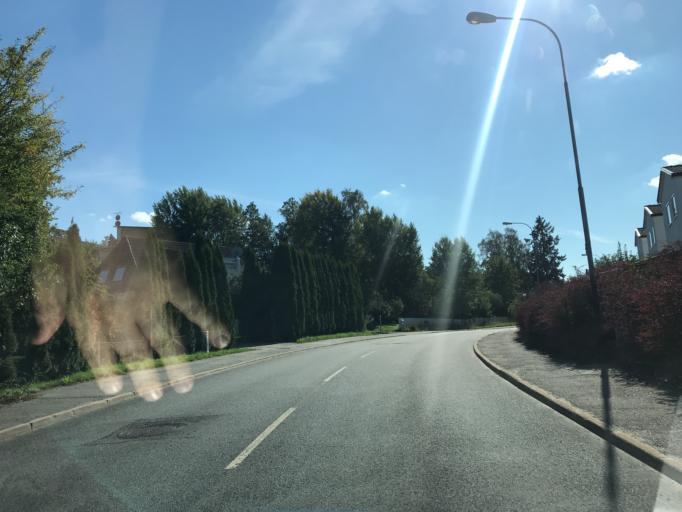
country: SE
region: Stockholm
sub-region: Sollentuna Kommun
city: Sollentuna
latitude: 59.4193
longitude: 17.9505
